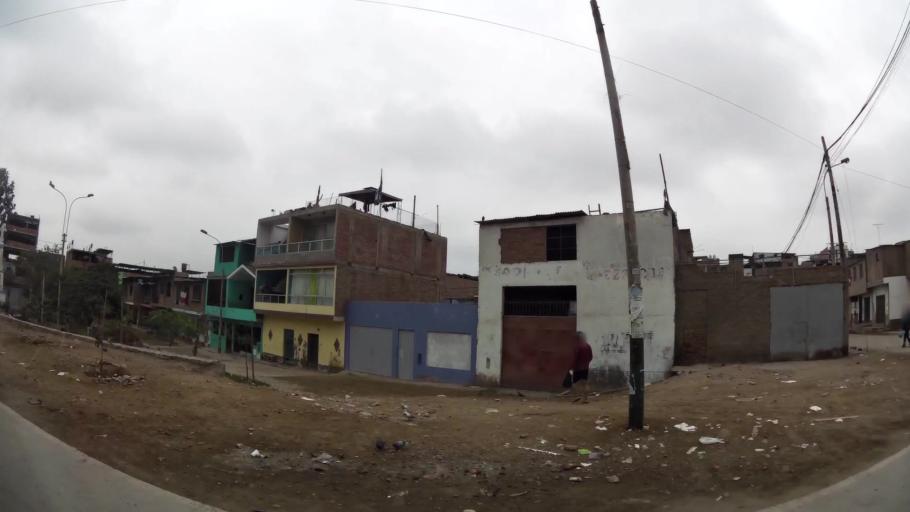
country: PE
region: Lima
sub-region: Lima
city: Surco
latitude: -12.1369
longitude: -76.9577
